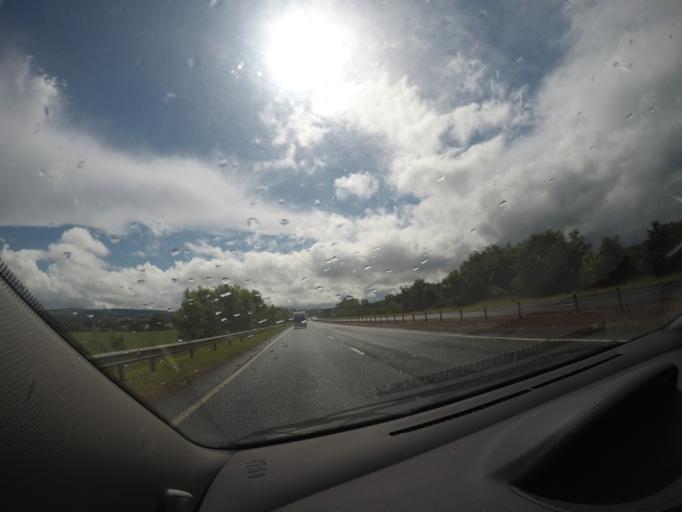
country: GB
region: Scotland
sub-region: Perth and Kinross
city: Auchterarder
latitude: 56.3019
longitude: -3.6741
